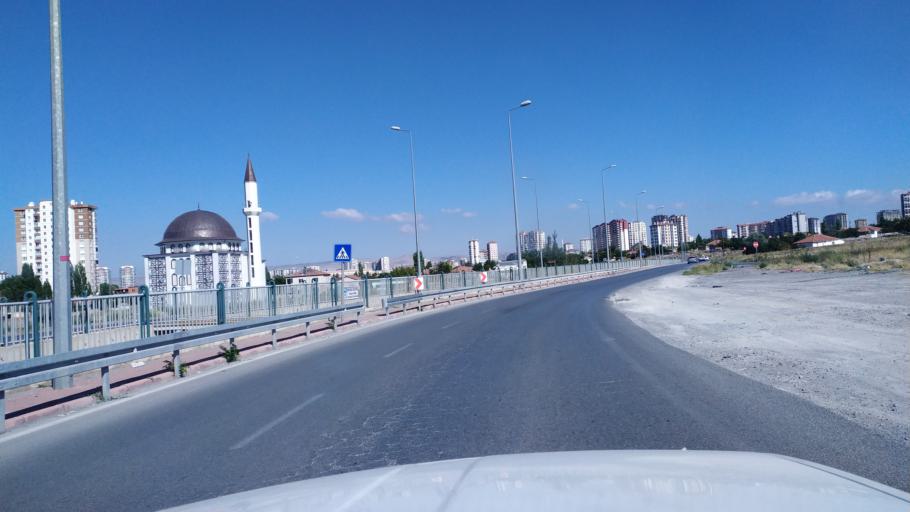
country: TR
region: Kayseri
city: Talas
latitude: 38.7302
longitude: 35.5494
